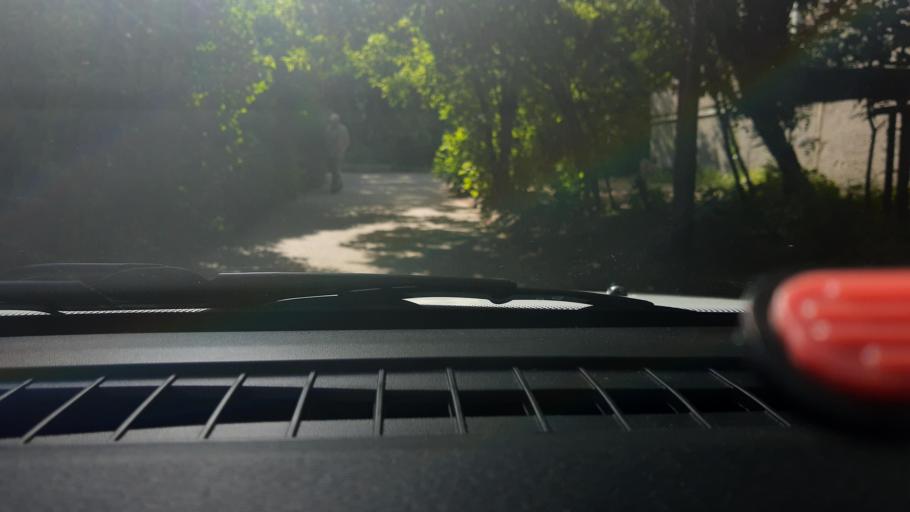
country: RU
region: Nizjnij Novgorod
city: Nizhniy Novgorod
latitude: 56.3031
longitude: 43.9292
